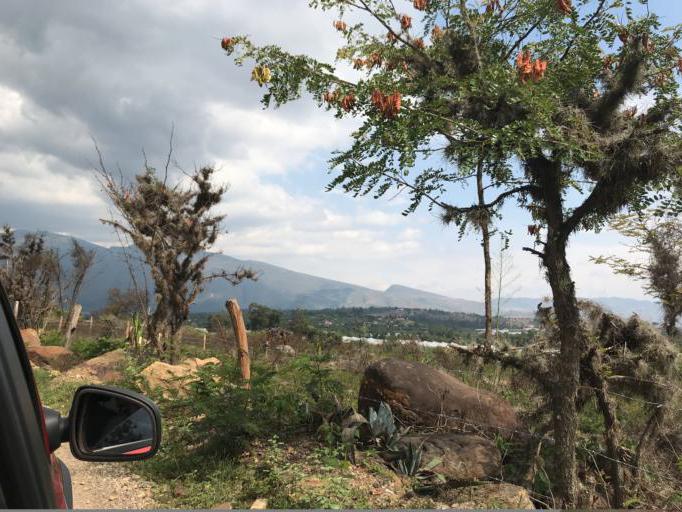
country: CO
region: Boyaca
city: Villa de Leiva
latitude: 5.6484
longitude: -73.5650
